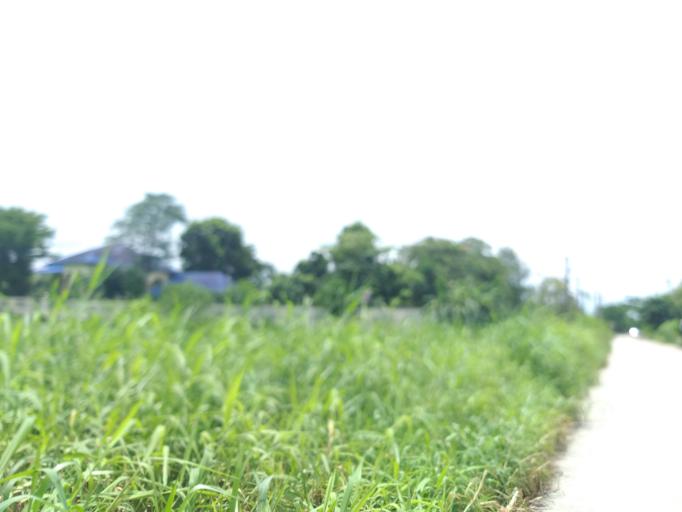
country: TH
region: Pathum Thani
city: Ban Lam Luk Ka
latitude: 14.0326
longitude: 100.8661
